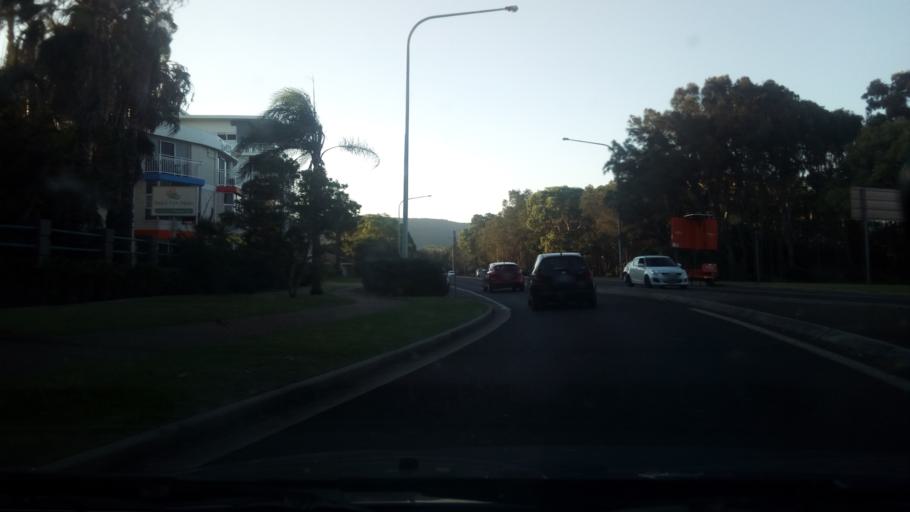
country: AU
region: New South Wales
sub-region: Wollongong
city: Wollongong
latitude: -34.4128
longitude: 150.8997
